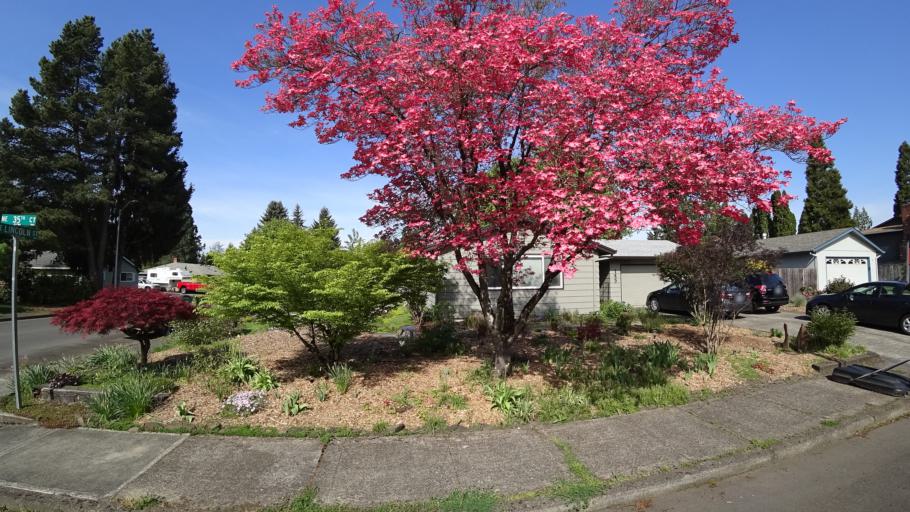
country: US
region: Oregon
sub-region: Washington County
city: Hillsboro
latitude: 45.5210
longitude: -122.9465
